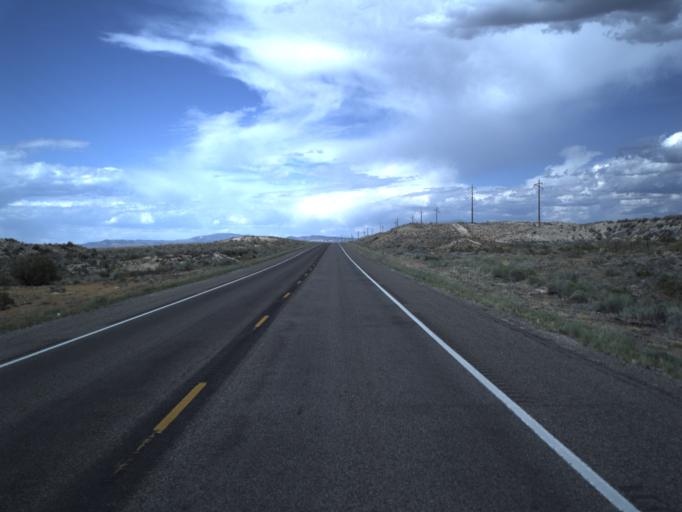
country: US
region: Utah
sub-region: Sevier County
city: Salina
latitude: 39.0125
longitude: -111.8359
